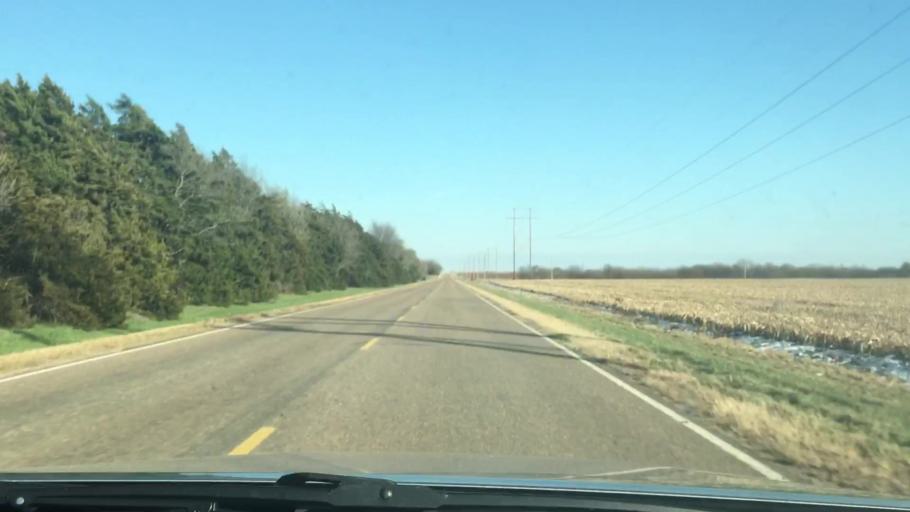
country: US
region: Kansas
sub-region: Rice County
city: Lyons
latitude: 38.2895
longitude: -98.1001
